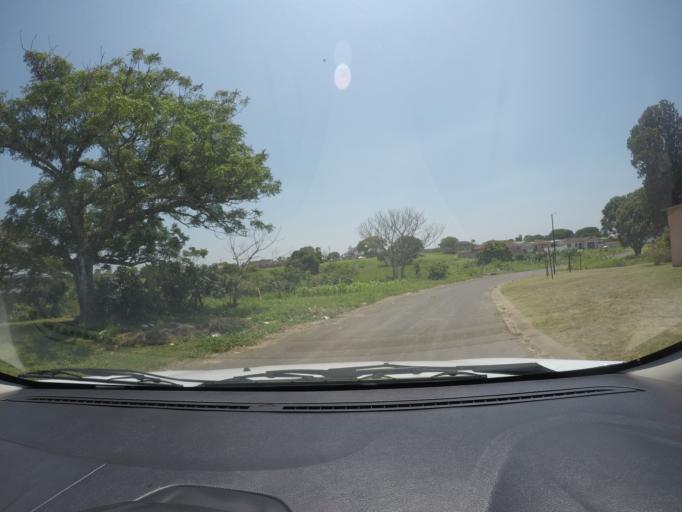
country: ZA
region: KwaZulu-Natal
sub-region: uThungulu District Municipality
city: eSikhawini
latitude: -28.8728
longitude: 31.9114
